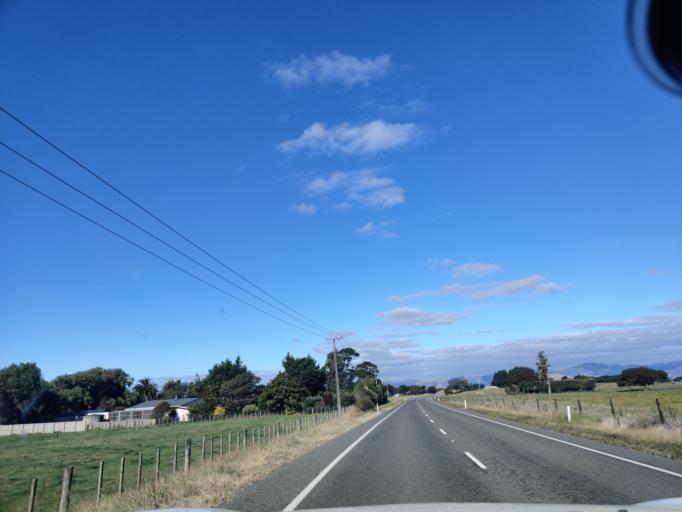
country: NZ
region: Manawatu-Wanganui
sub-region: Horowhenua District
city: Foxton
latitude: -40.4136
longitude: 175.3960
